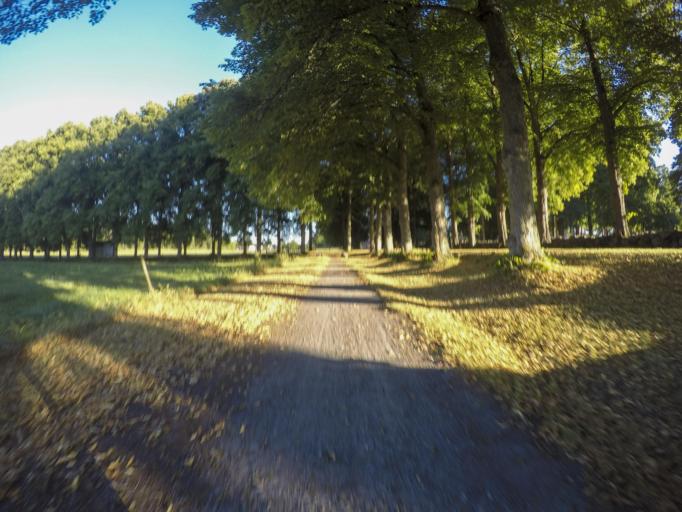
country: SE
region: Vaestmanland
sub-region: Vasteras
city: Vasteras
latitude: 59.5554
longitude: 16.6603
